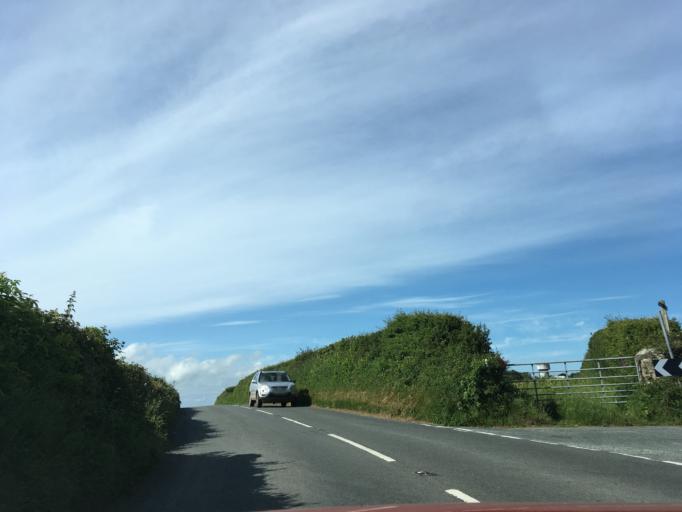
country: GB
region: England
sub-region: Devon
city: Dartmouth
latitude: 50.3398
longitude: -3.5898
